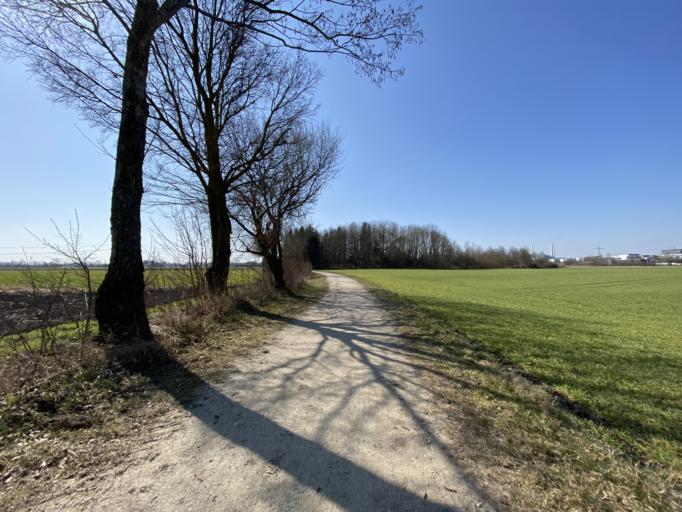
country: DE
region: Bavaria
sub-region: Upper Bavaria
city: Unterfoehring
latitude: 48.1906
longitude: 11.6638
